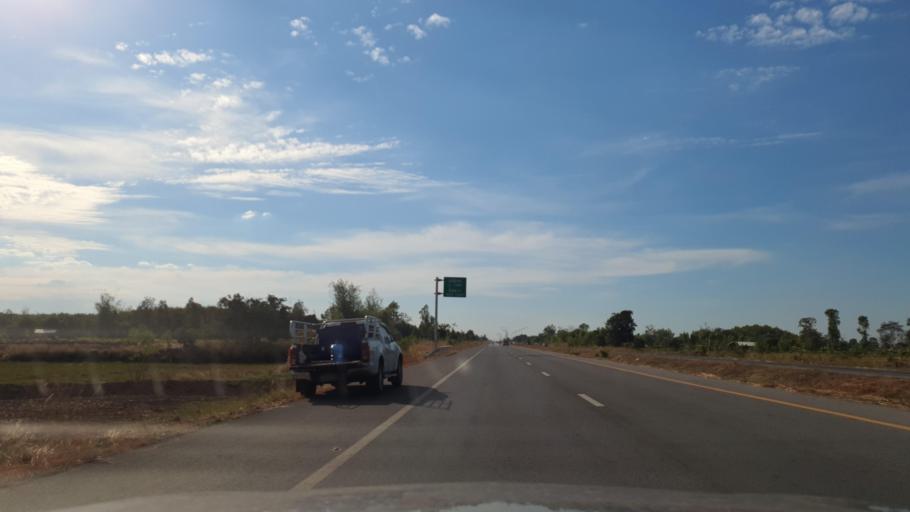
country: TH
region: Kalasin
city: Don Chan
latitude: 16.4109
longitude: 103.7417
